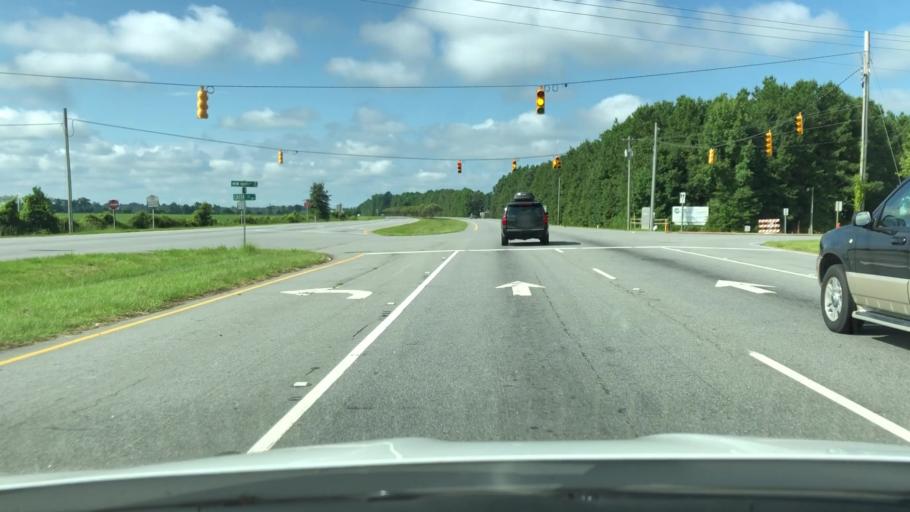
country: US
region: North Carolina
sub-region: Perquimans County
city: Hertford
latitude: 36.2047
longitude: -76.4475
